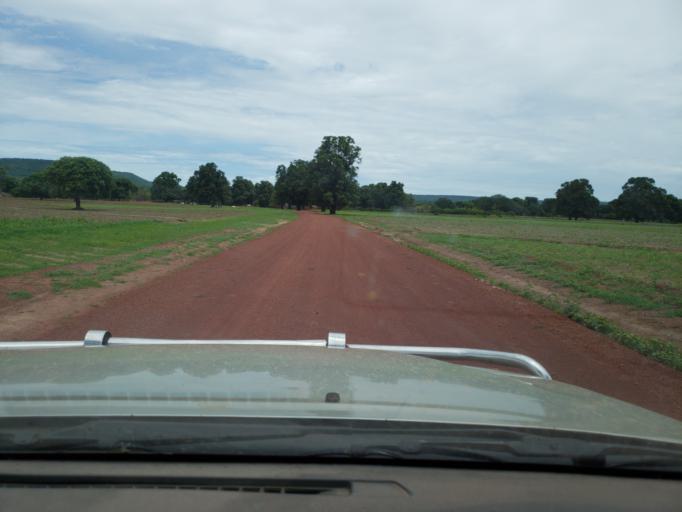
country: ML
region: Sikasso
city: Sikasso
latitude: 11.6713
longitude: -6.3401
